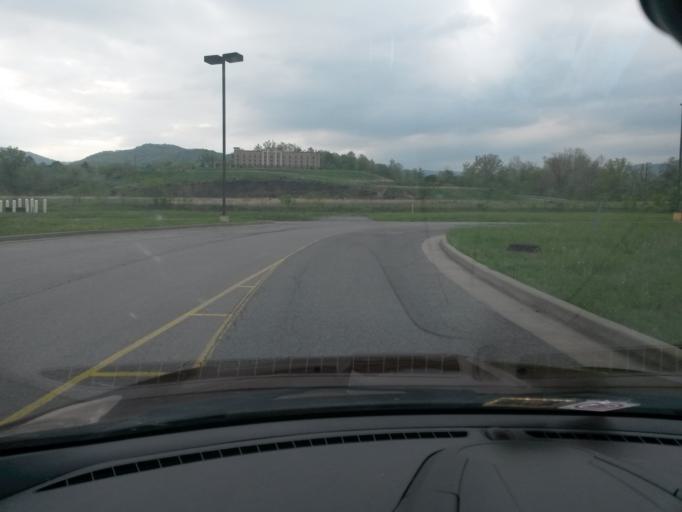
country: US
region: West Virginia
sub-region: Randolph County
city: Elkins
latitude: 38.8952
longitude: -79.8442
